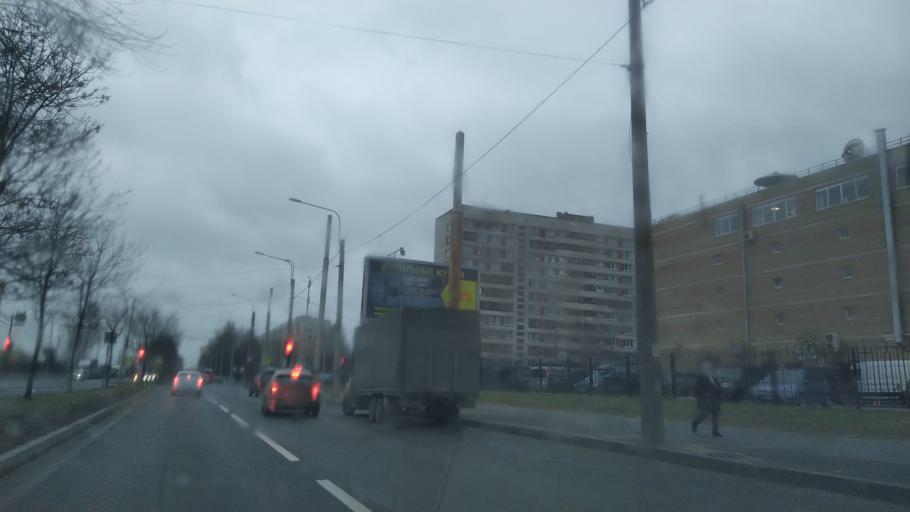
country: RU
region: St.-Petersburg
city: Grazhdanka
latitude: 60.0194
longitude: 30.4160
